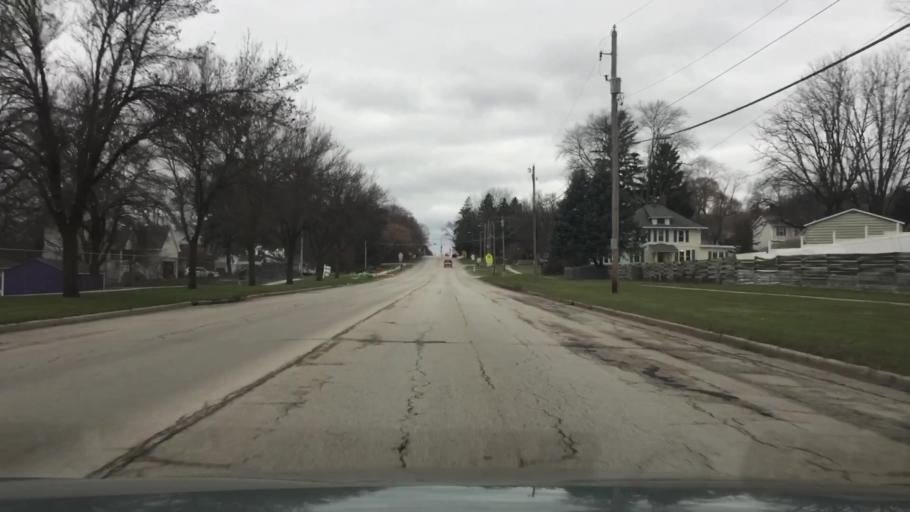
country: US
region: Wisconsin
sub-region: Waukesha County
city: Waukesha
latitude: 43.0217
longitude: -88.2634
